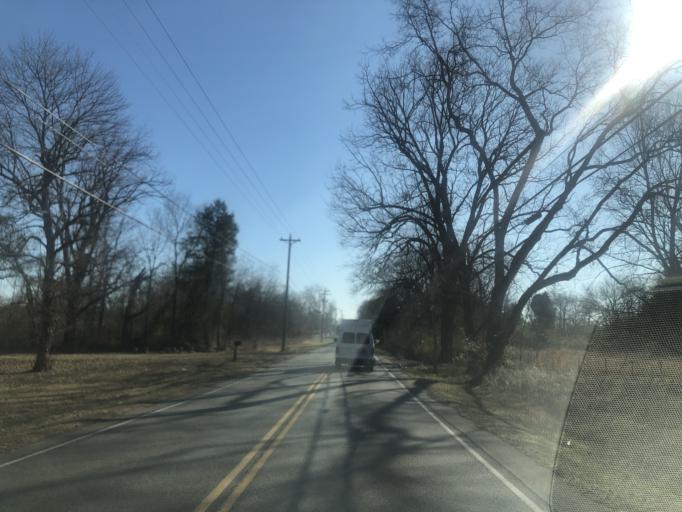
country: US
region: Tennessee
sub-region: Rutherford County
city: Smyrna
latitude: 35.9200
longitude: -86.4771
